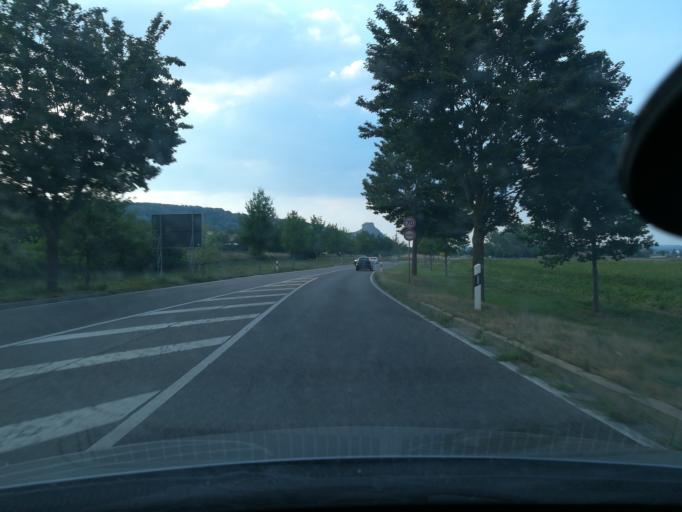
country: DE
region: Baden-Wuerttemberg
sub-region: Freiburg Region
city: Singen
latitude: 47.7727
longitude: 8.8241
